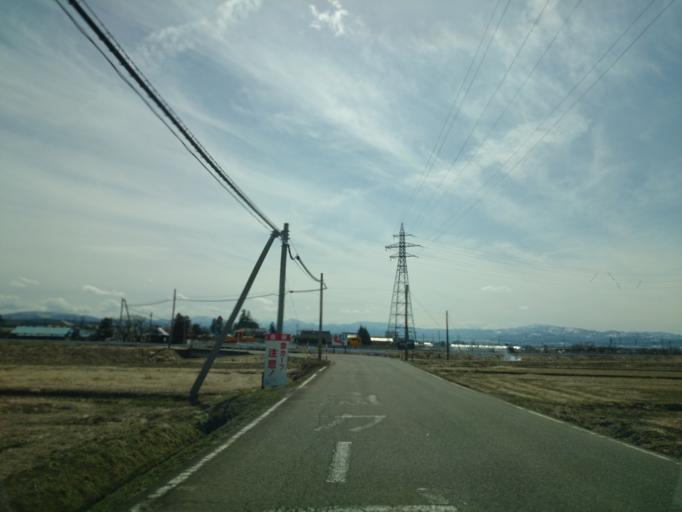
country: JP
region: Fukushima
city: Kitakata
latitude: 37.6471
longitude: 139.9103
